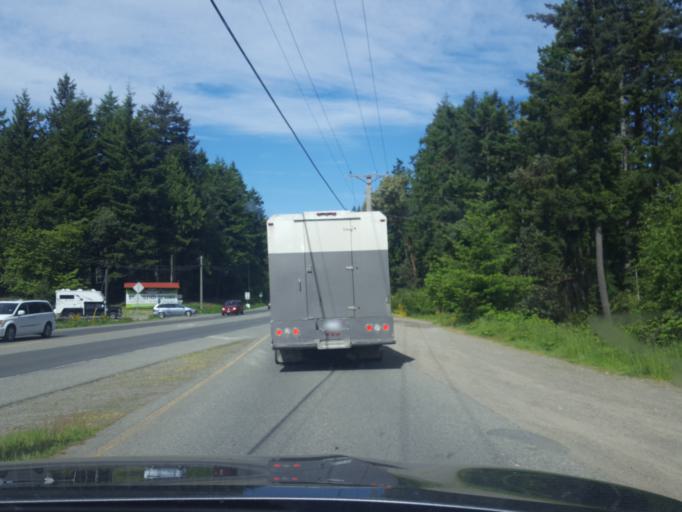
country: CA
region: British Columbia
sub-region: Regional District of Nanaimo
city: Parksville
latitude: 49.3147
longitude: -124.2770
